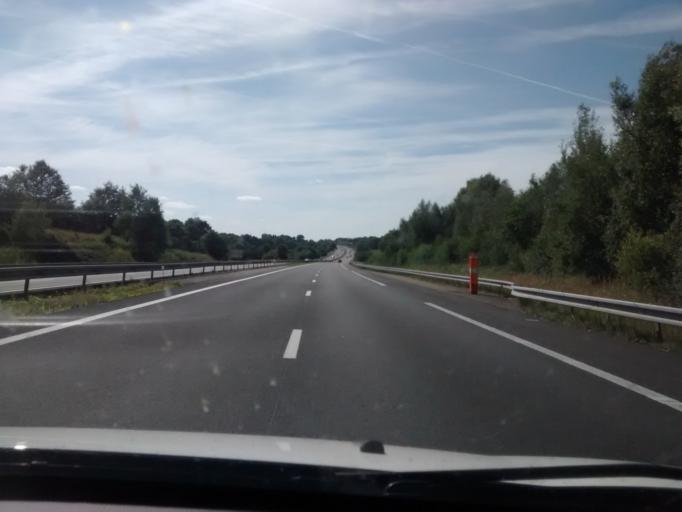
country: FR
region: Pays de la Loire
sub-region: Departement de la Mayenne
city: Vaiges
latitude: 48.0527
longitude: -0.4689
